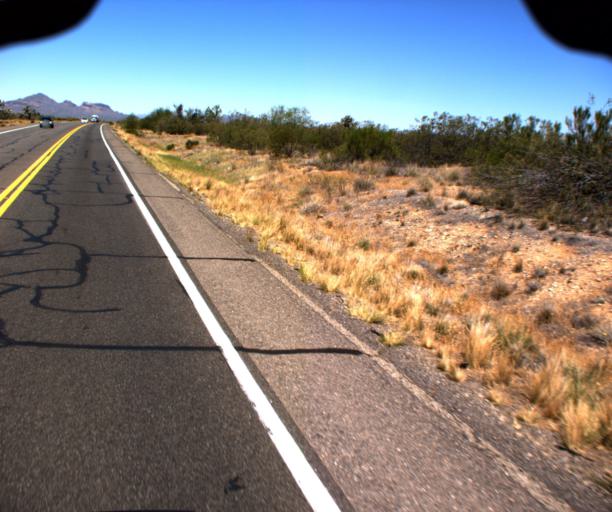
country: US
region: Arizona
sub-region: Yavapai County
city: Congress
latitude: 34.1851
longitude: -113.0446
